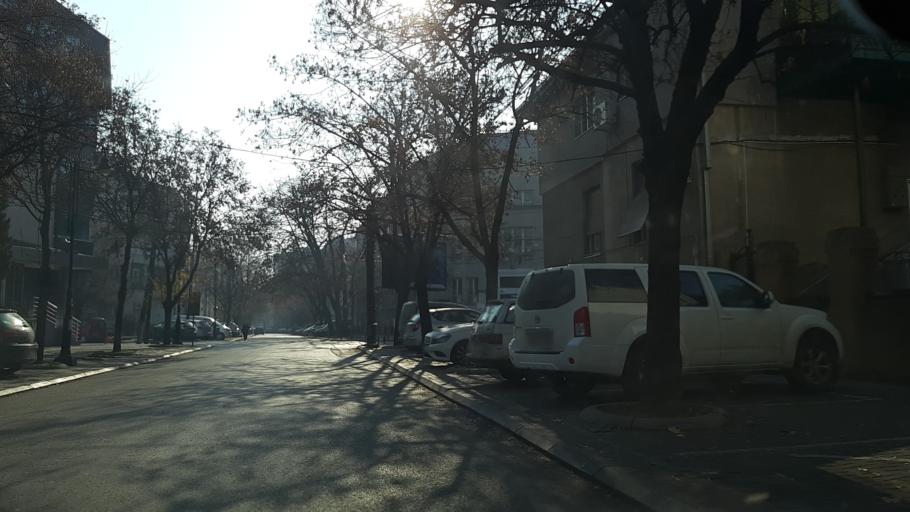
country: MK
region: Karpos
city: Skopje
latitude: 42.0010
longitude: 21.4218
